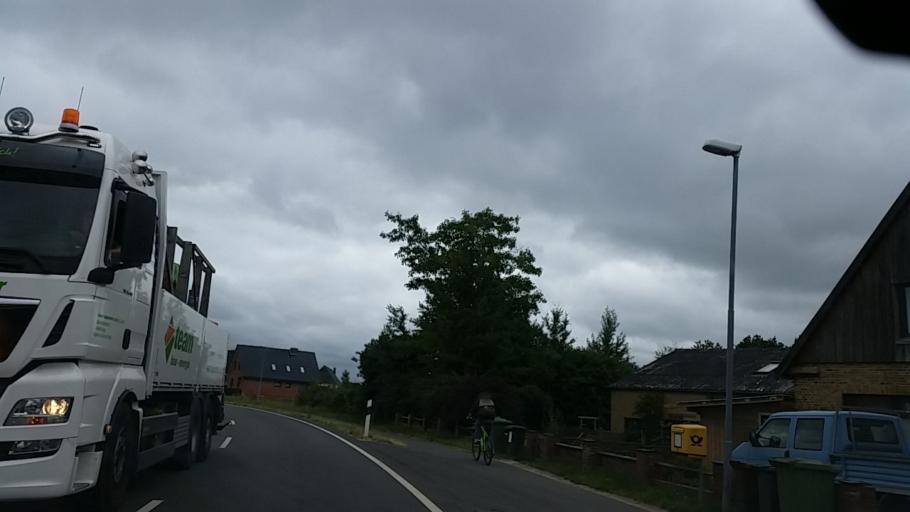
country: DE
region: Schleswig-Holstein
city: Dannewerk
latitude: 54.4936
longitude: 9.5150
